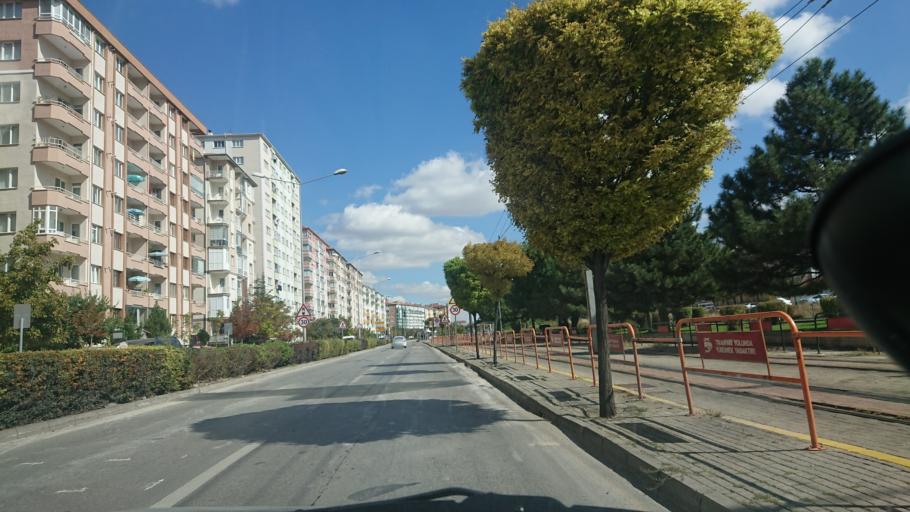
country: TR
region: Eskisehir
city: Eskisehir
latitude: 39.7674
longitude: 30.5413
